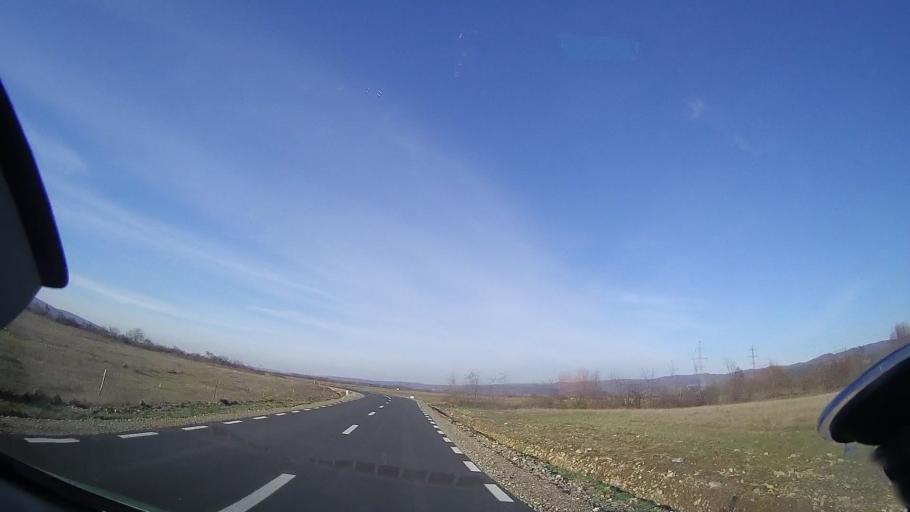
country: RO
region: Bihor
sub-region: Comuna Auseu
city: Auseu
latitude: 47.0118
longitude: 22.4997
